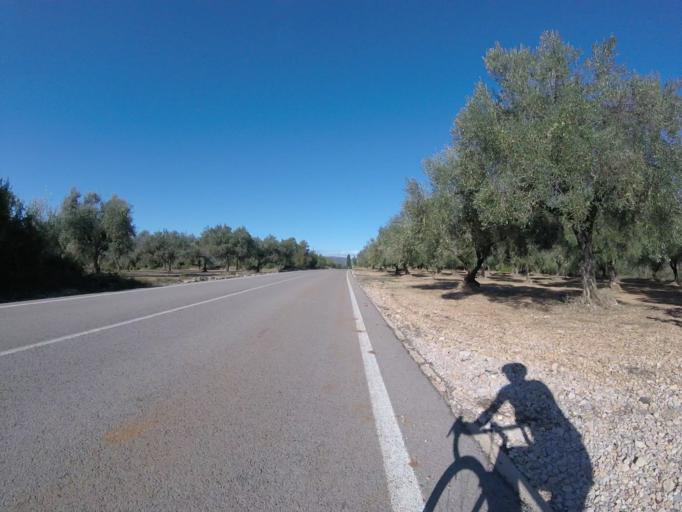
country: ES
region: Valencia
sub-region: Provincia de Castello
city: Cervera del Maestre
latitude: 40.4755
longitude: 0.2268
